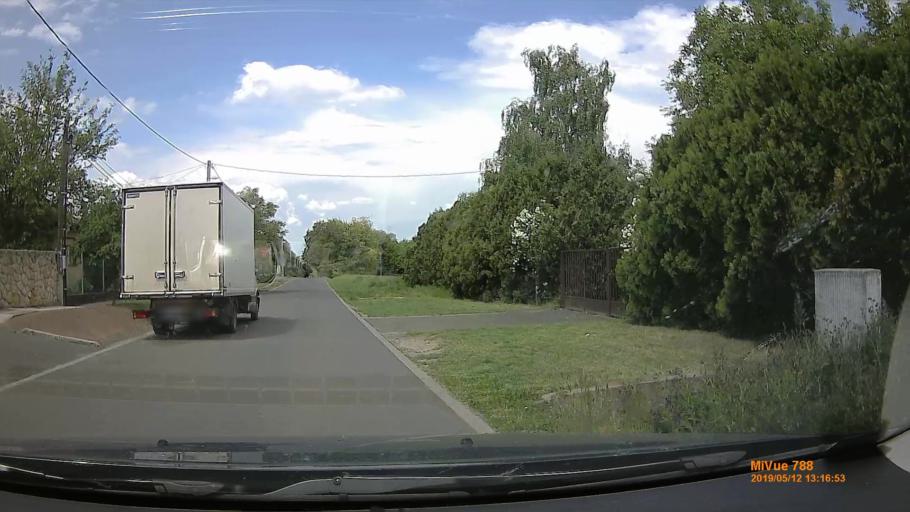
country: HU
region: Budapest
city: Budapest XVII. keruelet
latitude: 47.4792
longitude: 19.2891
